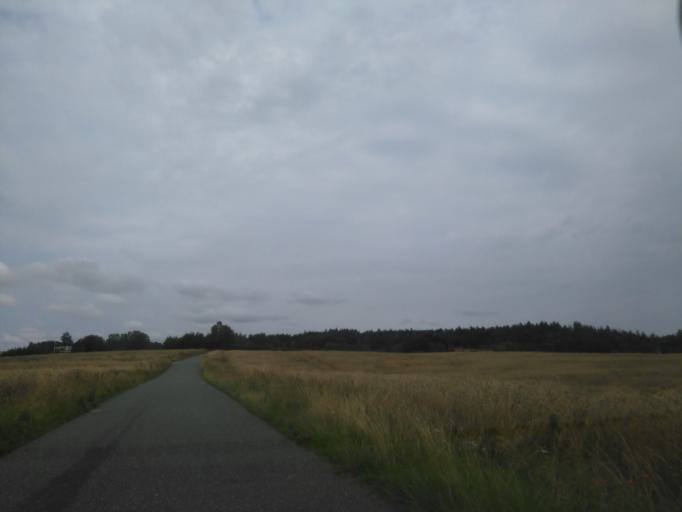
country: DK
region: Central Jutland
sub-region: Odder Kommune
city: Odder
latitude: 55.8880
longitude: 10.0454
